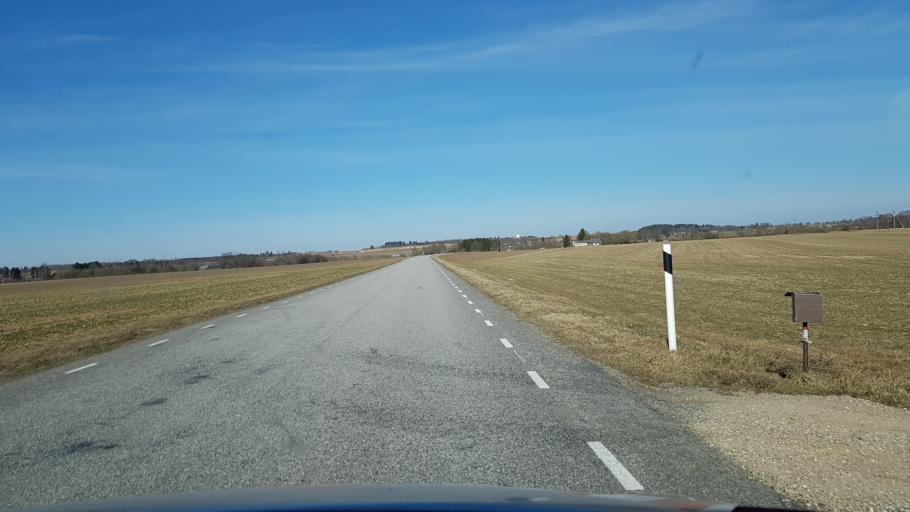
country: EE
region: Laeaene-Virumaa
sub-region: Vaeike-Maarja vald
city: Vaike-Maarja
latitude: 59.0608
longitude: 26.4699
